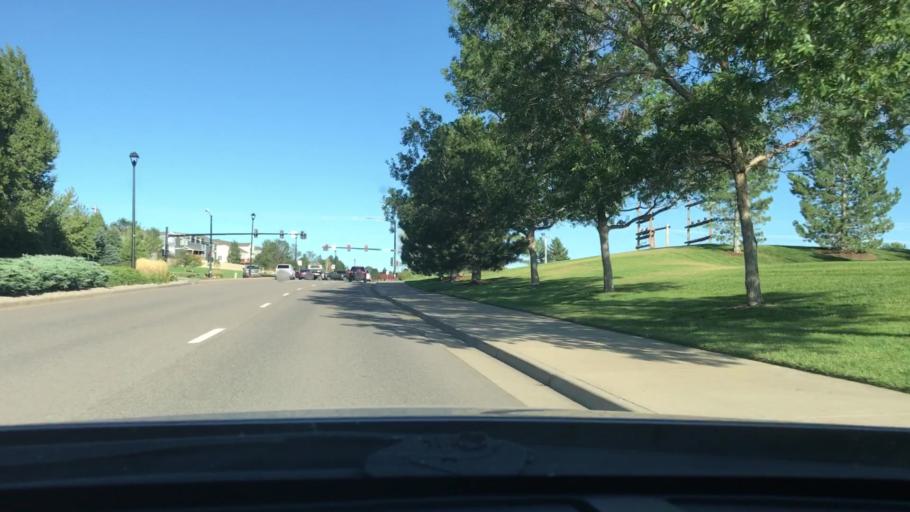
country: US
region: Colorado
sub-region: Arapahoe County
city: Dove Valley
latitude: 39.6095
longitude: -104.7746
